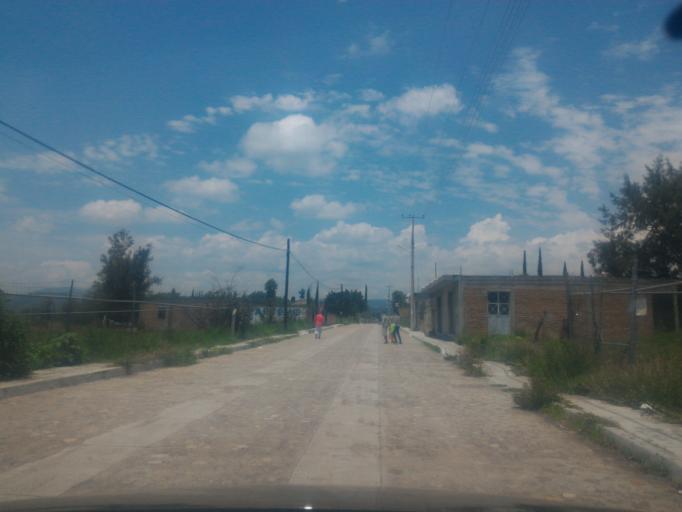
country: MX
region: Guanajuato
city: Ciudad Manuel Doblado
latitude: 20.8022
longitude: -101.9935
